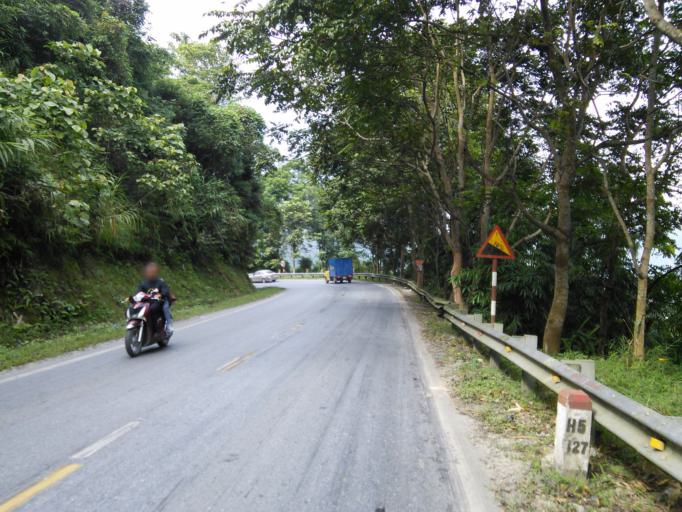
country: VN
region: Lao Cai
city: Lao Cai
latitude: 22.4462
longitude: 103.9372
